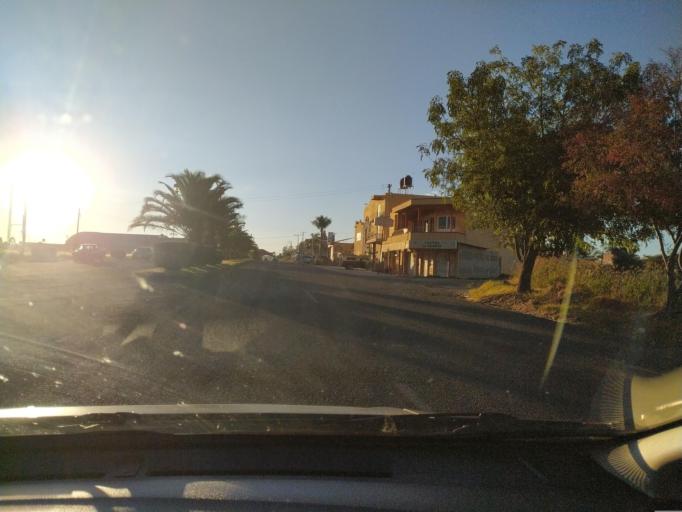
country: MX
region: Jalisco
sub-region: San Julian
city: Colonia Veintitres de Mayo
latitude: 21.0129
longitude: -102.1925
